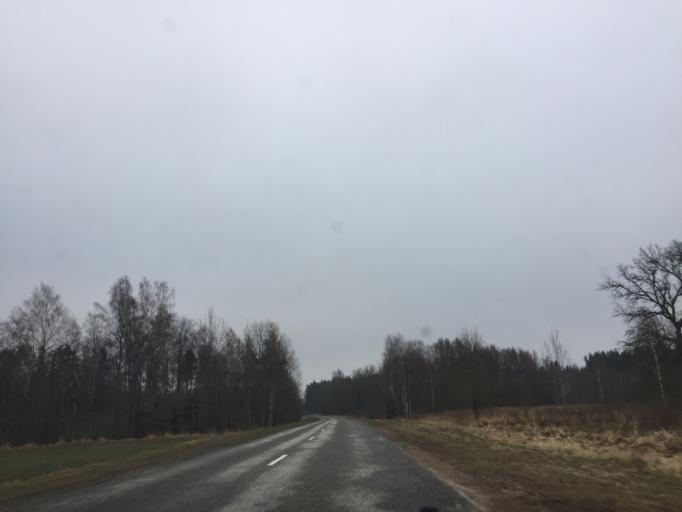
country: LV
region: Limbazu Rajons
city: Limbazi
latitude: 57.5477
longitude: 24.6745
